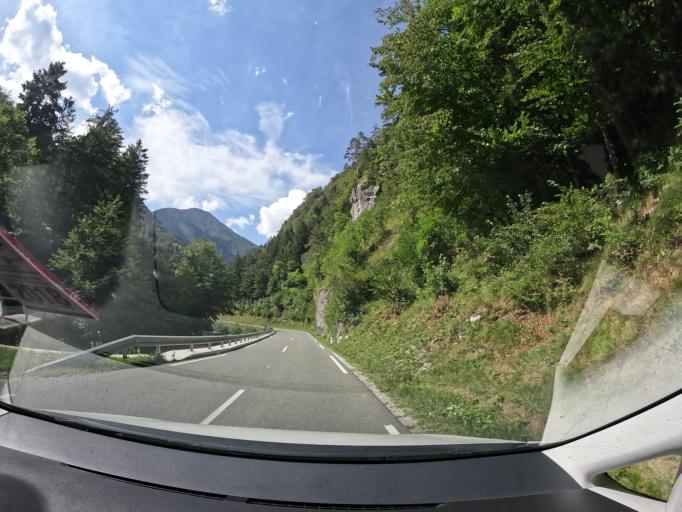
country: SI
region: Jezersko
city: Zgornje Jezersko
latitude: 46.3616
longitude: 14.4566
